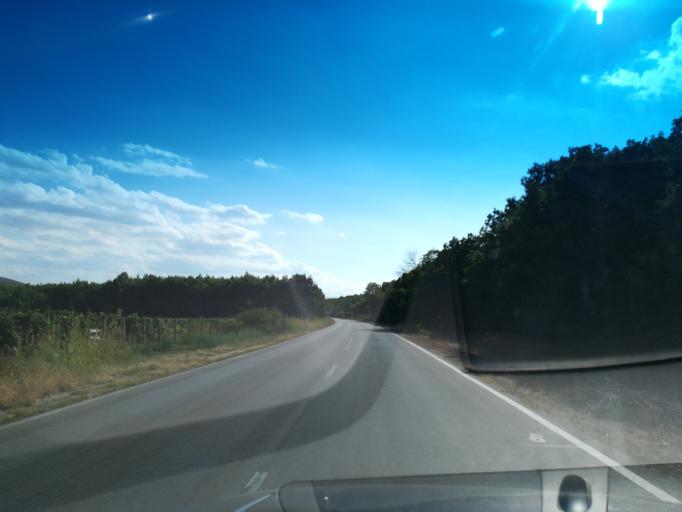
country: BG
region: Khaskovo
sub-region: Obshtina Mineralni Bani
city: Mineralni Bani
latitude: 41.9986
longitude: 25.3667
